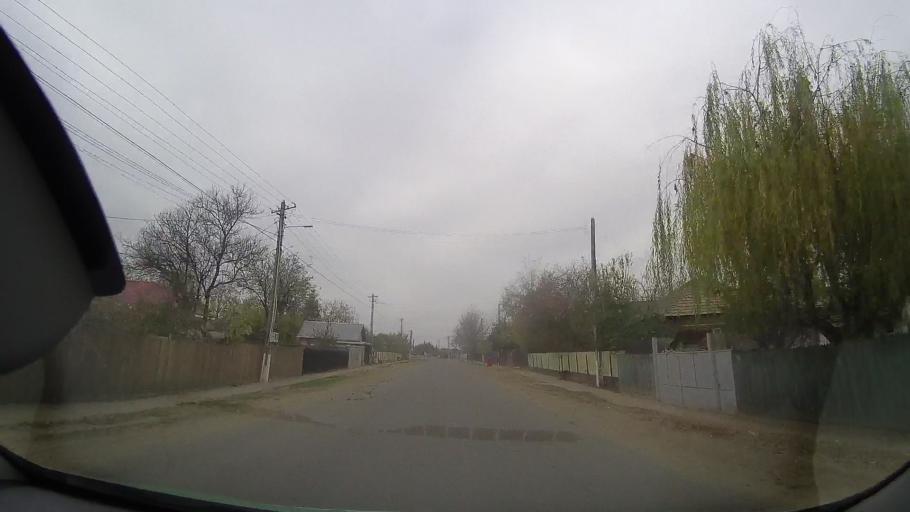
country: RO
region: Buzau
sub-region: Comuna Luciu
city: Luciu
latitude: 44.9727
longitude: 27.0755
